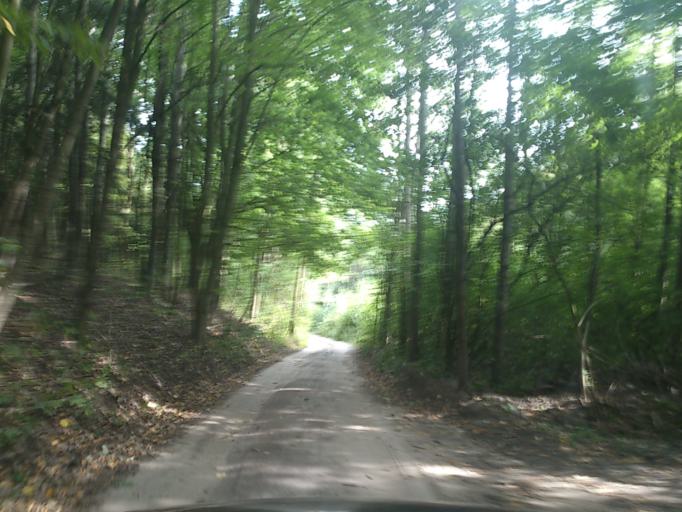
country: PL
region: Kujawsko-Pomorskie
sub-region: Powiat golubsko-dobrzynski
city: Golub-Dobrzyn
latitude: 53.1231
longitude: 19.0637
